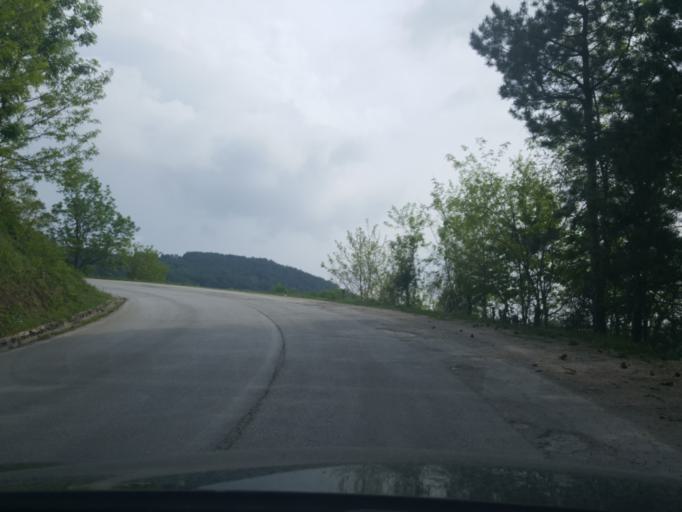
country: RS
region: Central Serbia
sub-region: Zlatiborski Okrug
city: Bajina Basta
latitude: 44.0773
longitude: 19.6638
